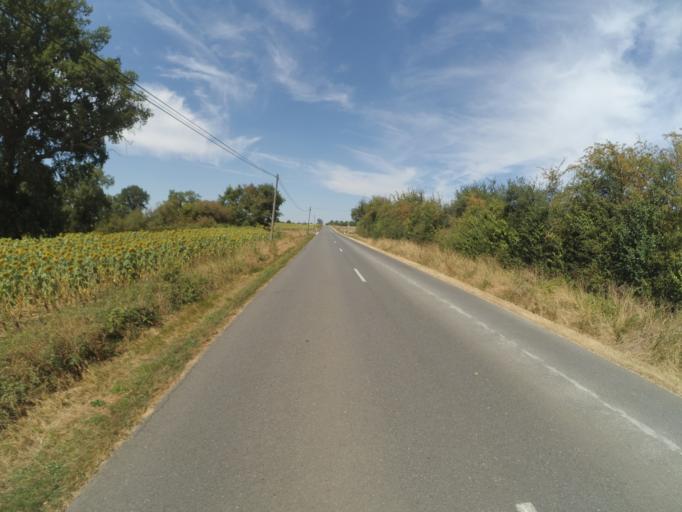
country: FR
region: Poitou-Charentes
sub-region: Departement de la Vienne
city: Availles-Limouzine
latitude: 46.1622
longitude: 0.5495
